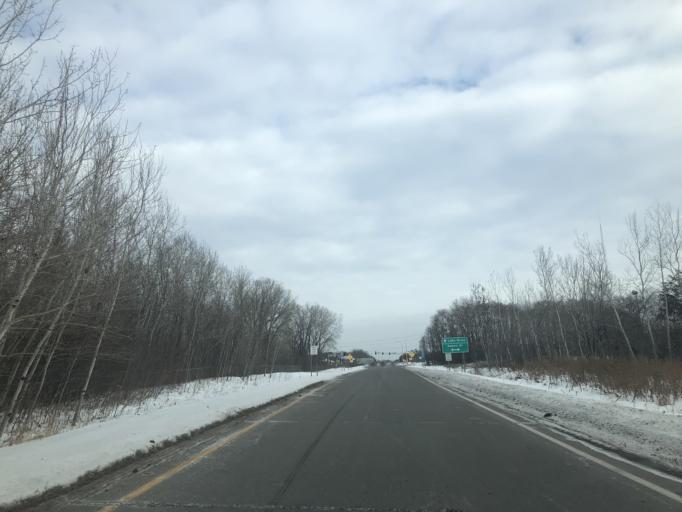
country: US
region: Minnesota
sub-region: Anoka County
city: Lexington
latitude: 45.1271
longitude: -93.1870
